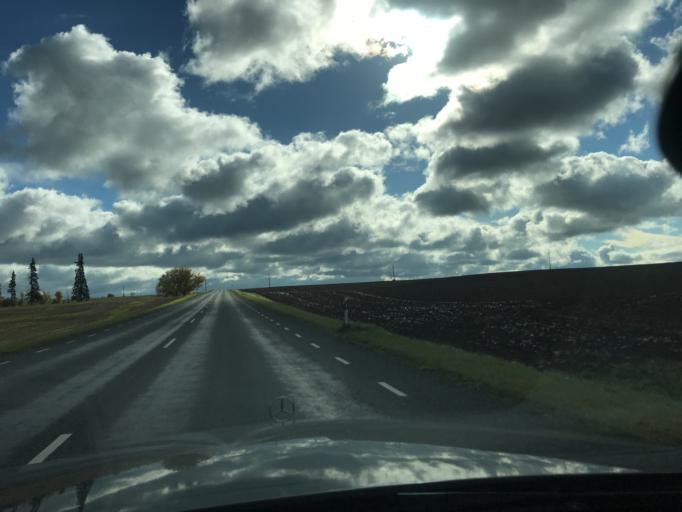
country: EE
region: Vorumaa
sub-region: Antsla vald
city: Vana-Antsla
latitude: 57.9213
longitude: 26.3459
